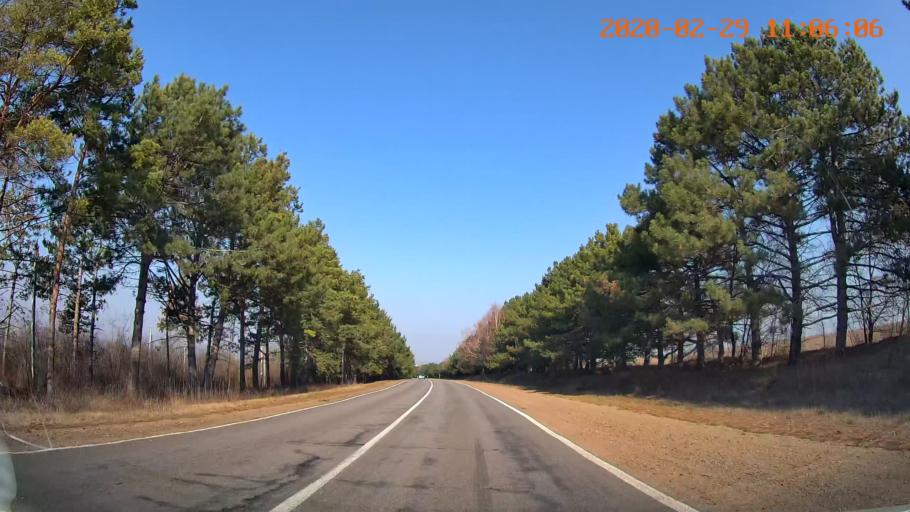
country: MD
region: Criuleni
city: Criuleni
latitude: 47.2104
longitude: 29.1896
